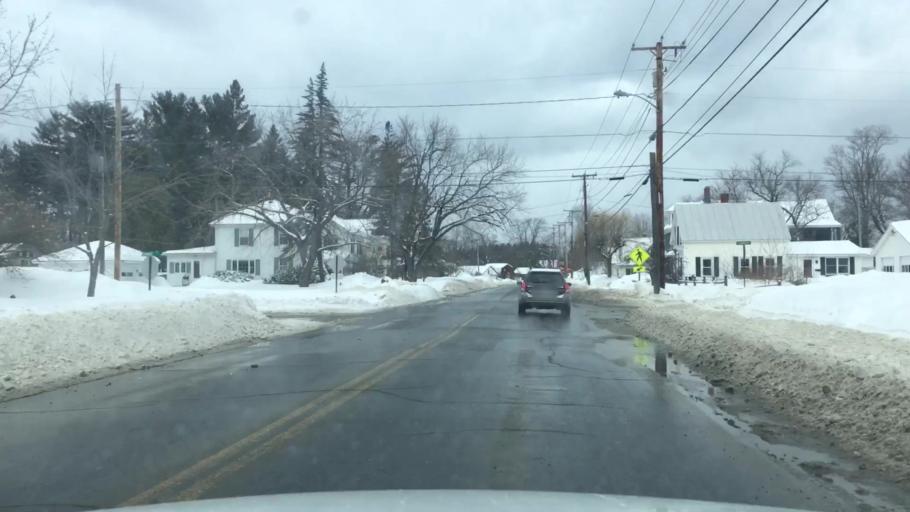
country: US
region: Maine
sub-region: Somerset County
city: Skowhegan
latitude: 44.7755
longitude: -69.7193
